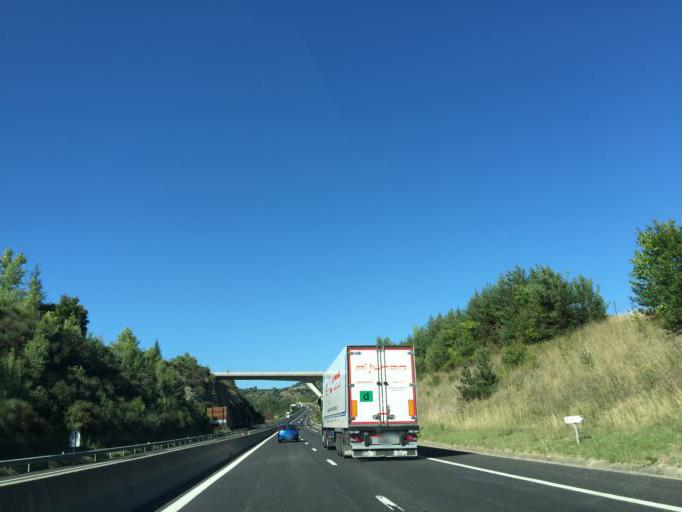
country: FR
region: Languedoc-Roussillon
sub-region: Departement de la Lozere
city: La Canourgue
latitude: 44.4637
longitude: 3.1929
